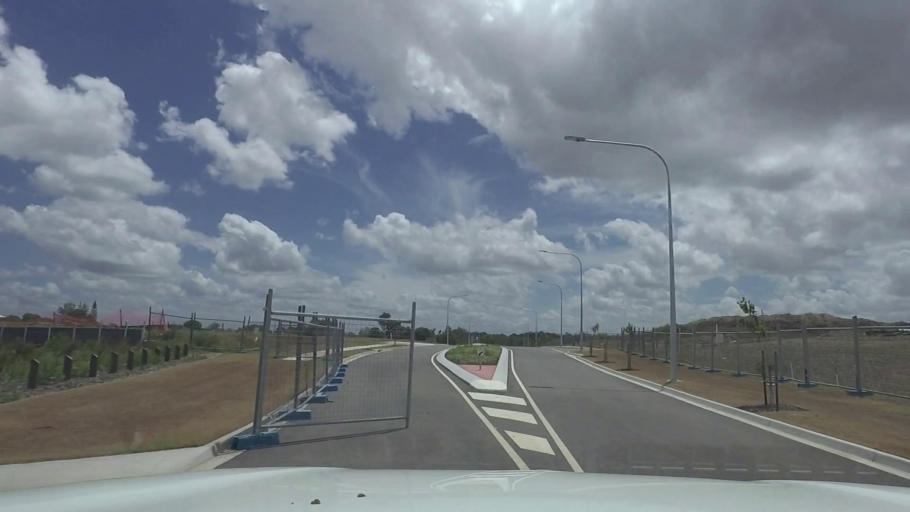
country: AU
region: Queensland
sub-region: Logan
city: Waterford West
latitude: -27.7072
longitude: 153.1200
